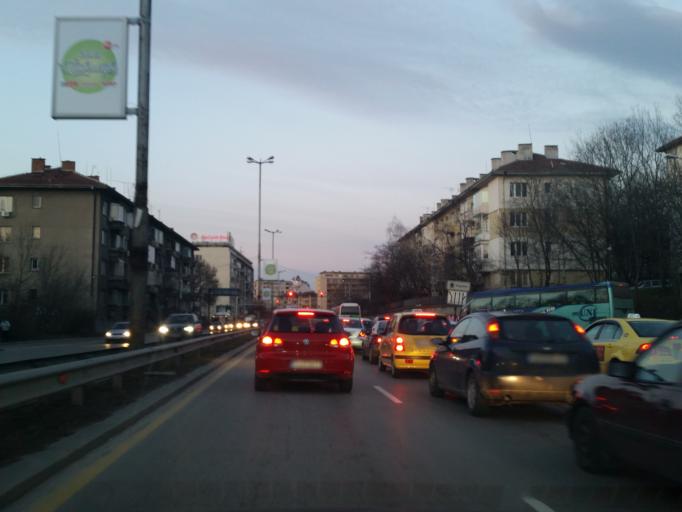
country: BG
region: Sofia-Capital
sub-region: Stolichna Obshtina
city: Sofia
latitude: 42.6844
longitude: 23.3488
